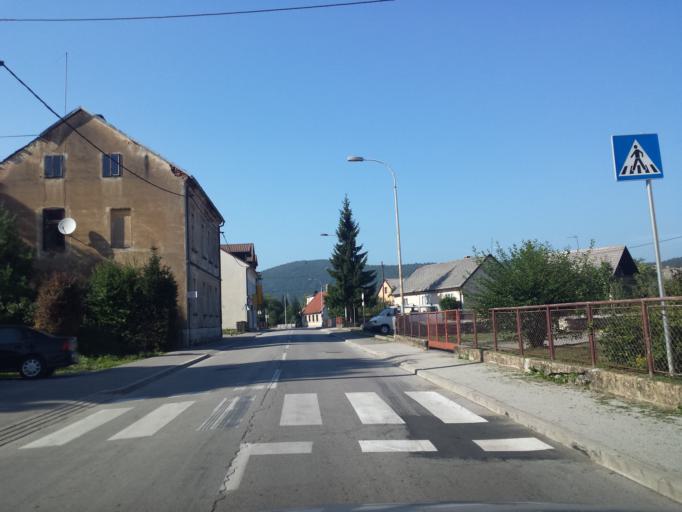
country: HR
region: Karlovacka
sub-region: Grad Ogulin
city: Ogulin
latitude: 45.2638
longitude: 15.2298
